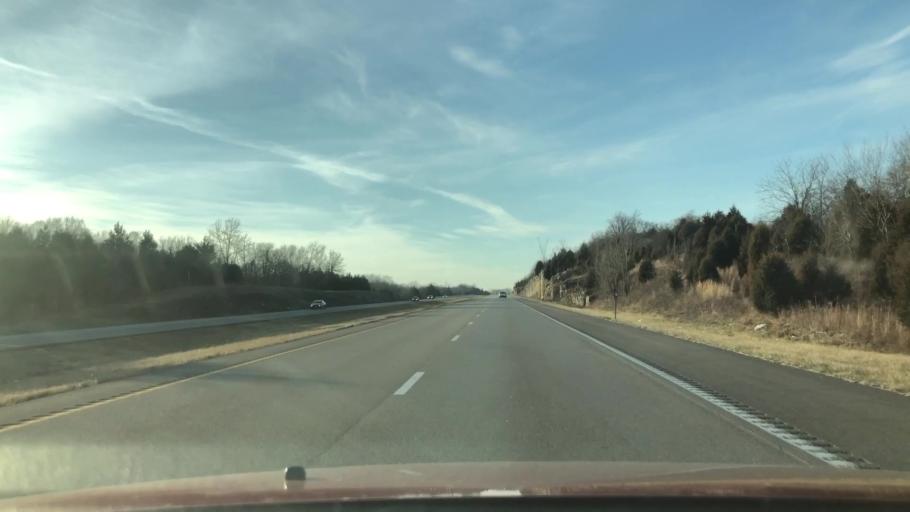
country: US
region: Missouri
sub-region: Wright County
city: Mansfield
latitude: 37.1121
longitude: -92.6578
